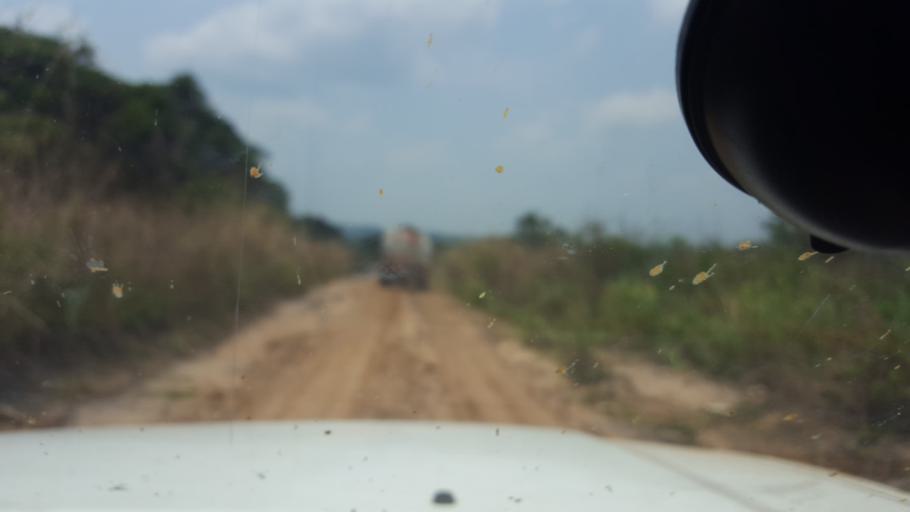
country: CD
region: Bandundu
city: Mushie
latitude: -3.7515
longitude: 16.6398
